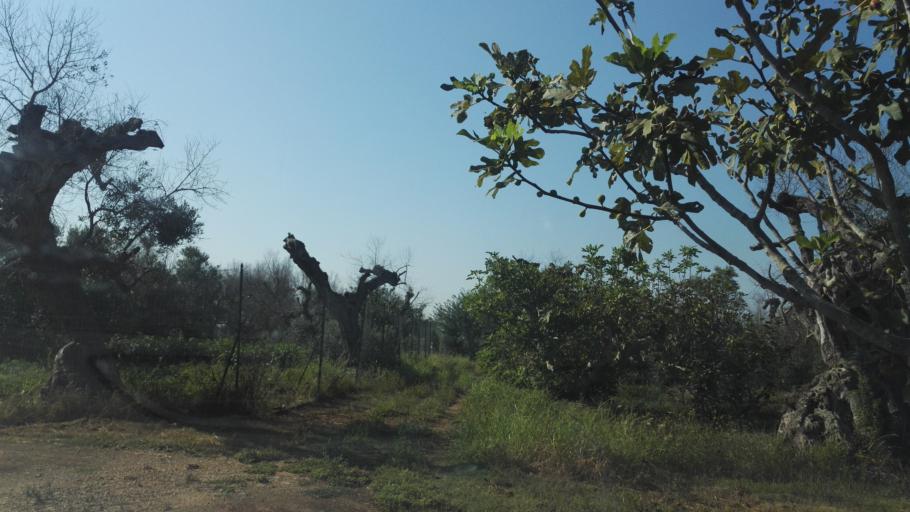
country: IT
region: Apulia
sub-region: Provincia di Lecce
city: Alezio
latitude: 40.0492
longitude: 18.0390
